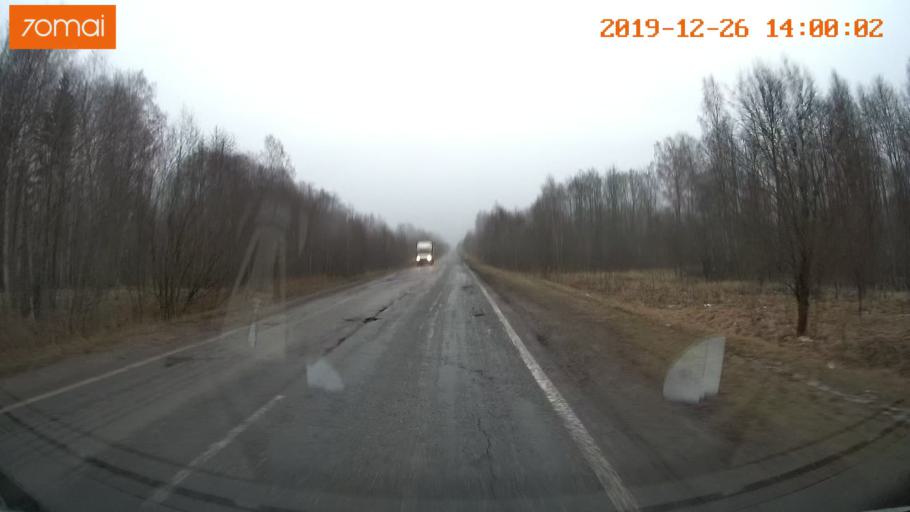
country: RU
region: Jaroslavl
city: Poshekhon'ye
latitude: 58.5610
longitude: 38.7357
